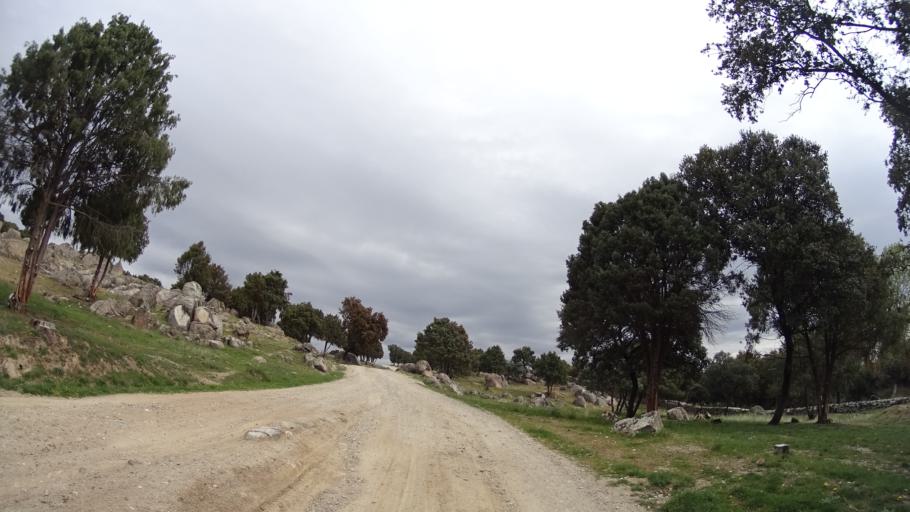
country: ES
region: Madrid
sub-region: Provincia de Madrid
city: Hoyo de Manzanares
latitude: 40.6030
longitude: -3.8789
